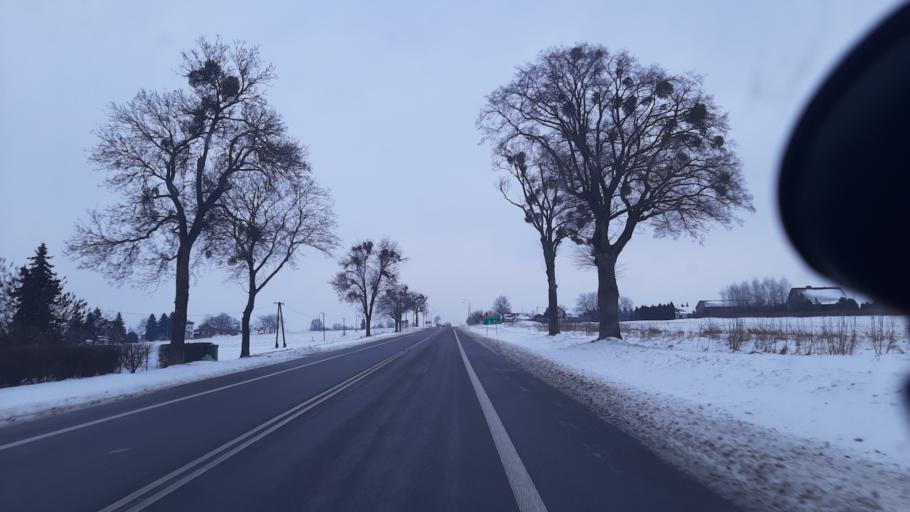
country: PL
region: Lublin Voivodeship
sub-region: Powiat pulawski
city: Markuszow
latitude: 51.3703
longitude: 22.2774
